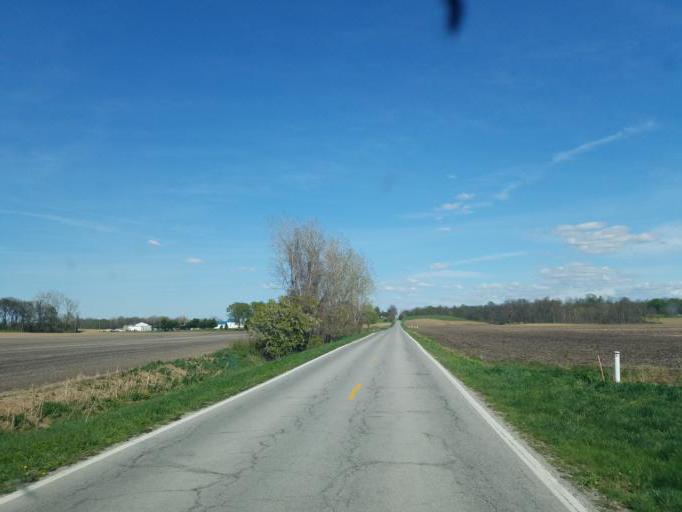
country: US
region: Ohio
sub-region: Huron County
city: Plymouth
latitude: 40.9956
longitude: -82.7122
